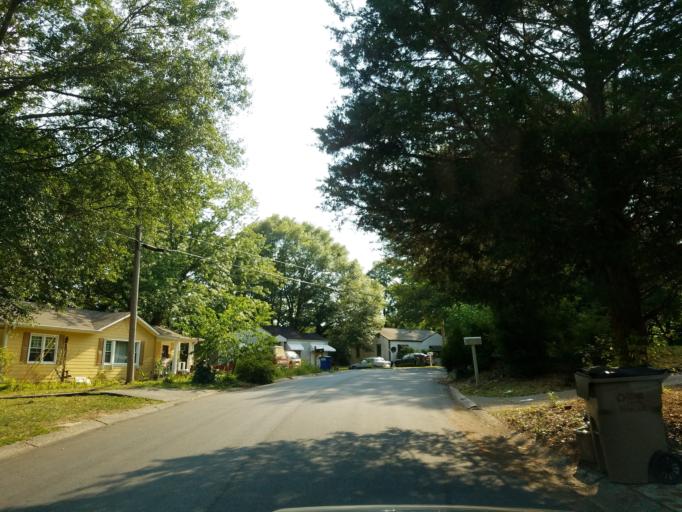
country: US
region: Georgia
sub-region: Cobb County
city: Marietta
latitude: 33.9456
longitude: -84.4965
